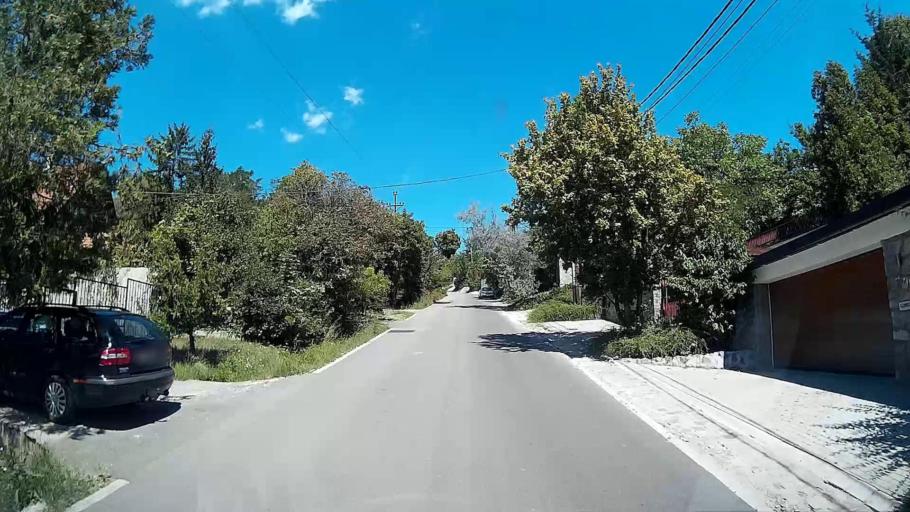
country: HU
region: Pest
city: Szentendre
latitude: 47.6925
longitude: 19.0841
